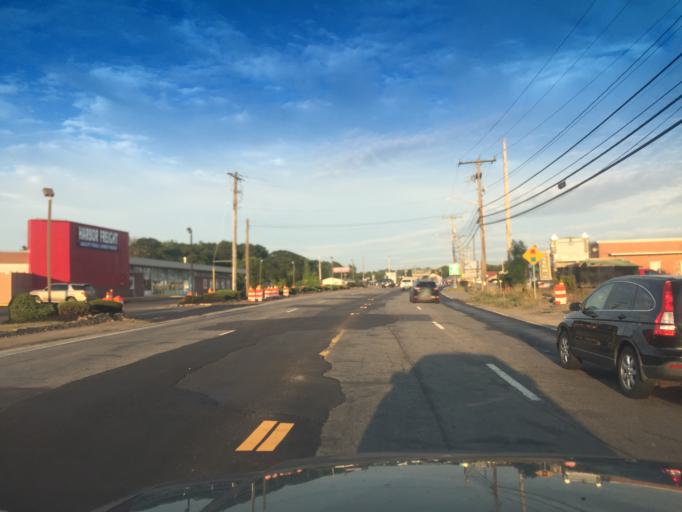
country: US
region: Massachusetts
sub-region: Plymouth County
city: Onset
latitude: 41.7568
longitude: -70.6524
